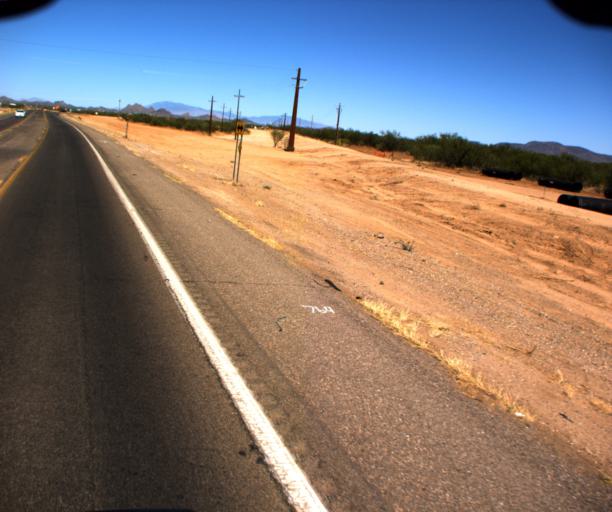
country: US
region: Arizona
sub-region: Pima County
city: Valencia West
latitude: 32.1332
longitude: -111.1737
